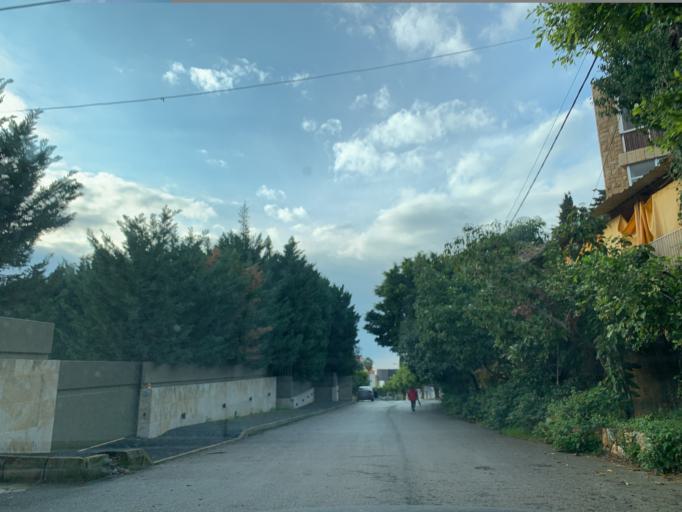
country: LB
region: Mont-Liban
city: Baabda
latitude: 33.8512
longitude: 35.5770
